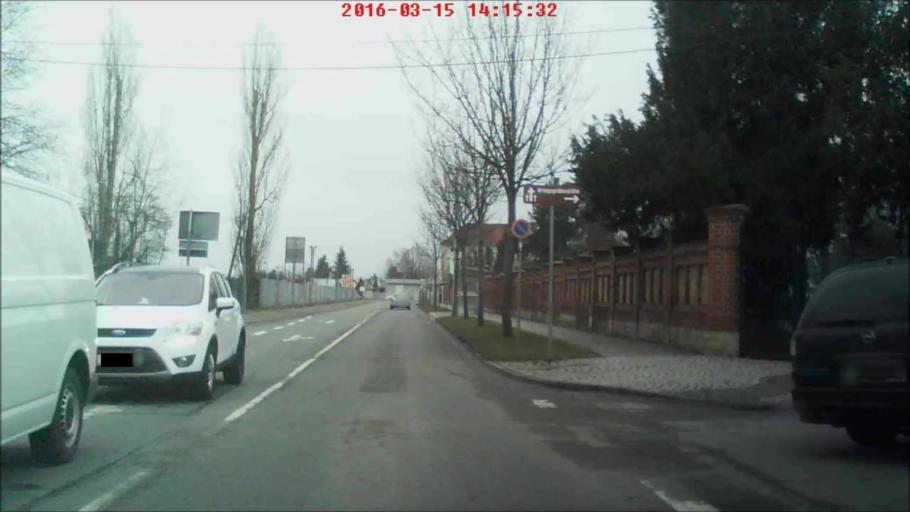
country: DE
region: Thuringia
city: Arnstadt
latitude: 50.8381
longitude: 10.9587
